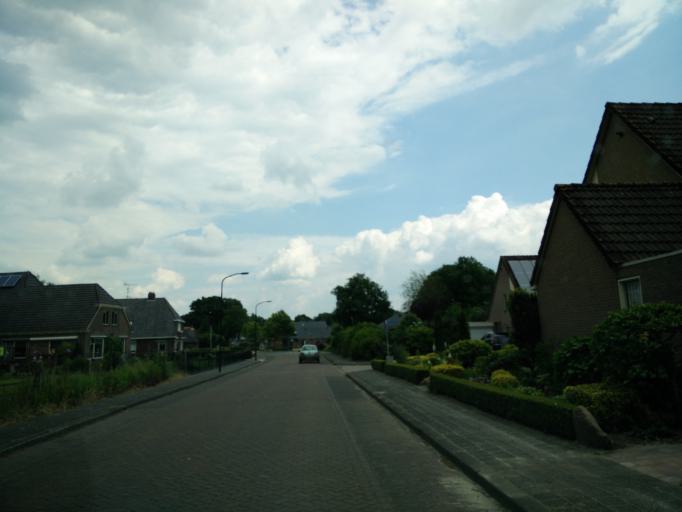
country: NL
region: Drenthe
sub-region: Gemeente Aa en Hunze
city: Anloo
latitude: 52.9866
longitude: 6.6511
